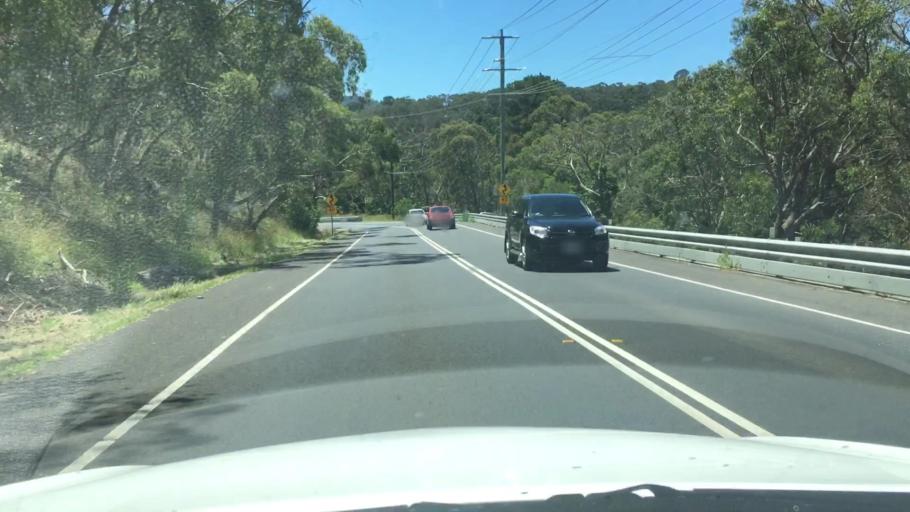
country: AU
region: Victoria
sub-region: Yarra Ranges
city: Belgrave Heights
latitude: -37.9268
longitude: 145.3624
